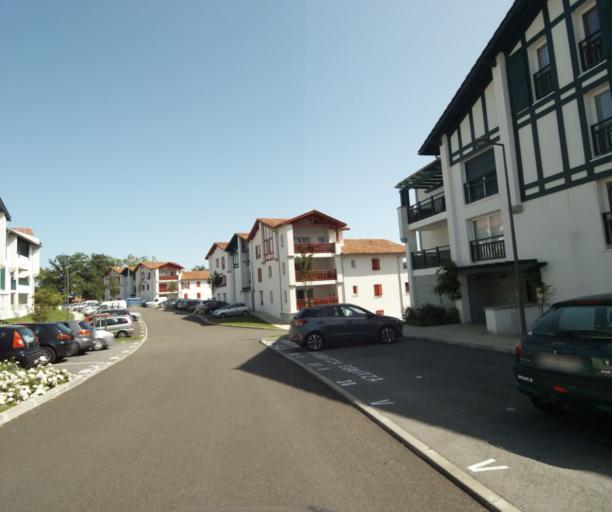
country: FR
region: Aquitaine
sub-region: Departement des Pyrenees-Atlantiques
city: Mouguerre
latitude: 43.4711
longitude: -1.4448
